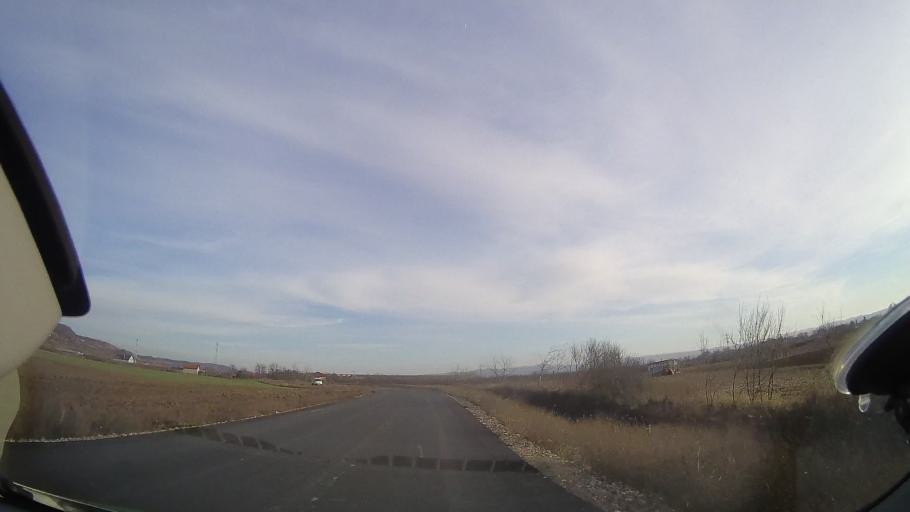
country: RO
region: Bihor
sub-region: Comuna Tileagd
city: Tileagd
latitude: 47.0826
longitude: 22.1913
